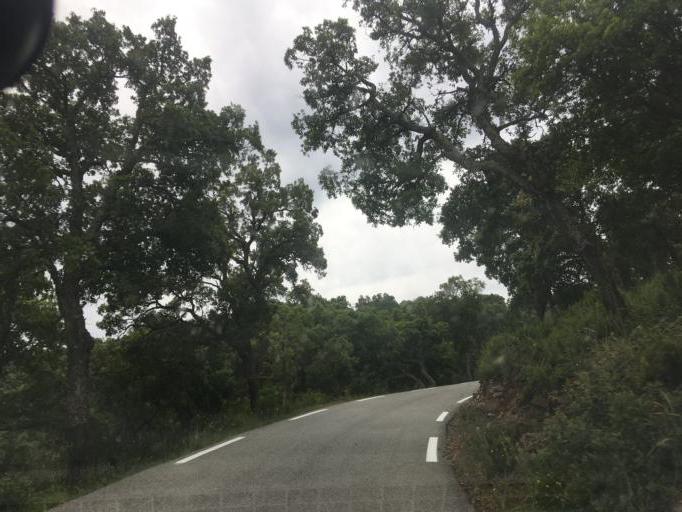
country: FR
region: Provence-Alpes-Cote d'Azur
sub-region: Departement du Var
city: Pierrefeu-du-Var
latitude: 43.2187
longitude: 6.2189
